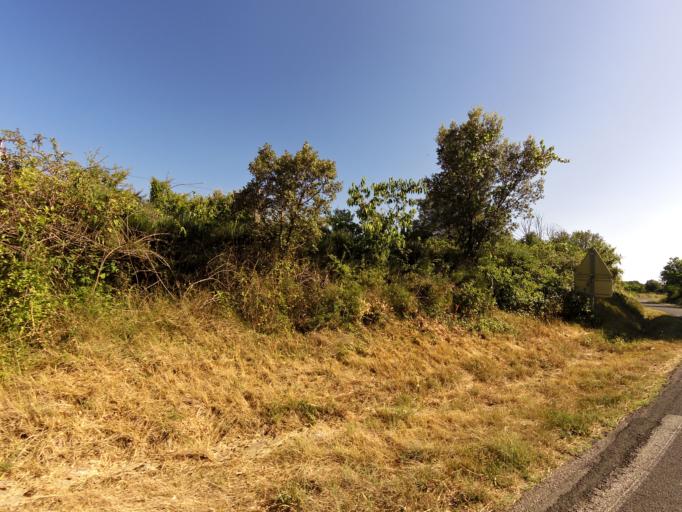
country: FR
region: Languedoc-Roussillon
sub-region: Departement de l'Herault
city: Boisseron
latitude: 43.7604
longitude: 4.0452
